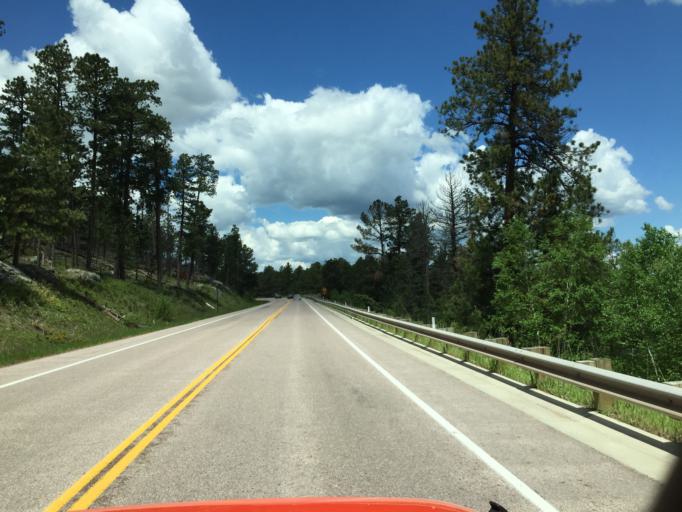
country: US
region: South Dakota
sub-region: Custer County
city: Custer
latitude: 43.8961
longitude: -103.5184
